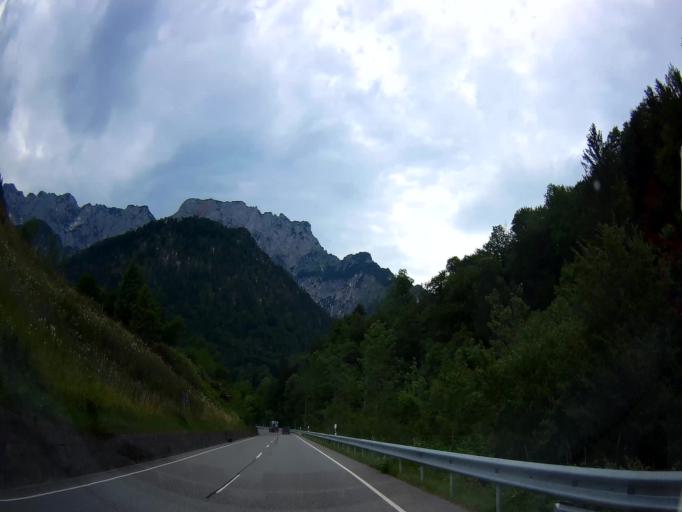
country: DE
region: Bavaria
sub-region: Upper Bavaria
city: Marktschellenberg
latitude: 47.7000
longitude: 13.0437
